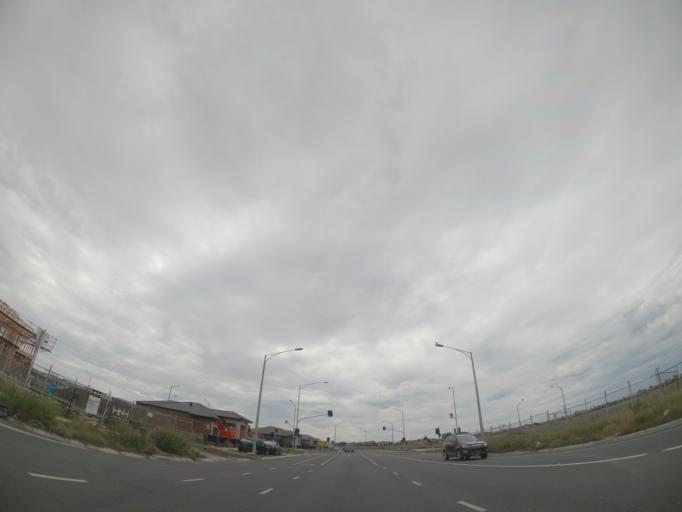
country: AU
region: Victoria
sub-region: Hume
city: Roxburgh Park
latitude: -37.5742
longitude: 144.8969
